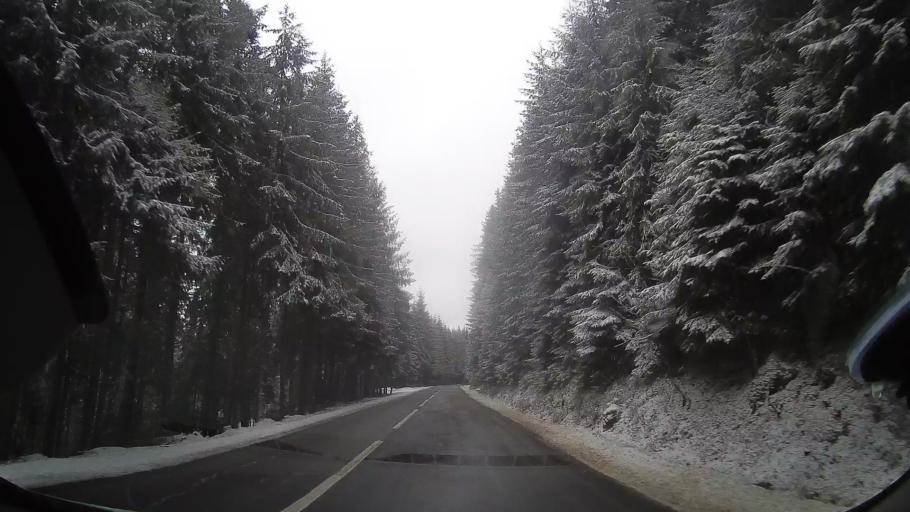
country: RO
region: Cluj
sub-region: Comuna Belis
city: Belis
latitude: 46.6522
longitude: 23.0446
